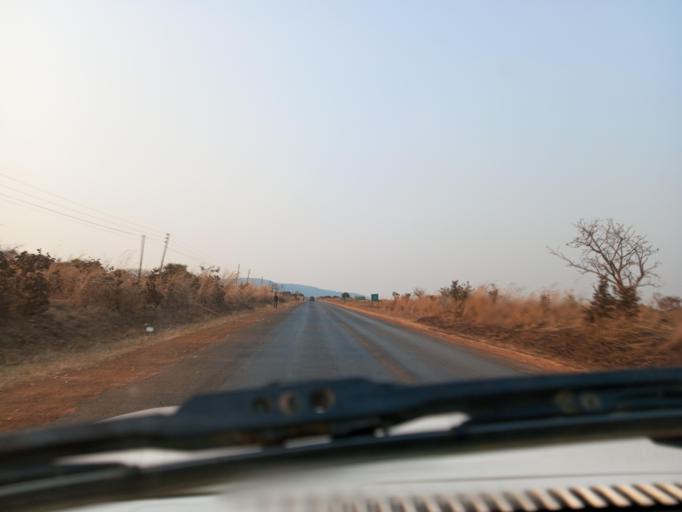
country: ZM
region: Northern
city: Mpika
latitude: -11.9099
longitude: 31.4150
